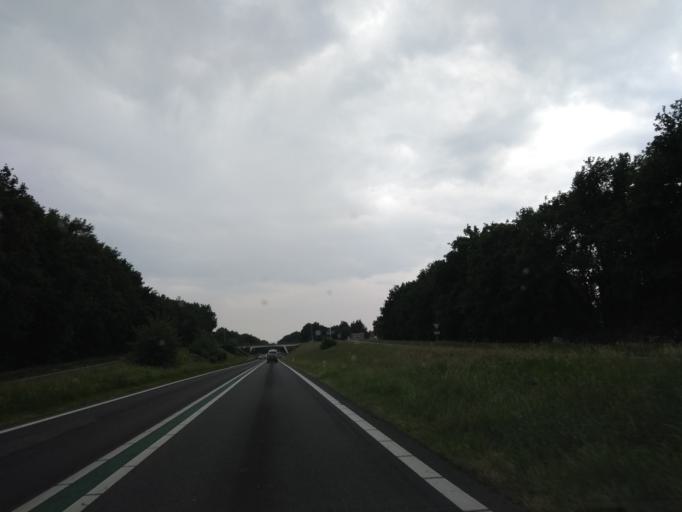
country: NL
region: Overijssel
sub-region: Gemeente Twenterand
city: Westerhaar-Vriezenveensewijk
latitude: 52.4688
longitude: 6.6236
